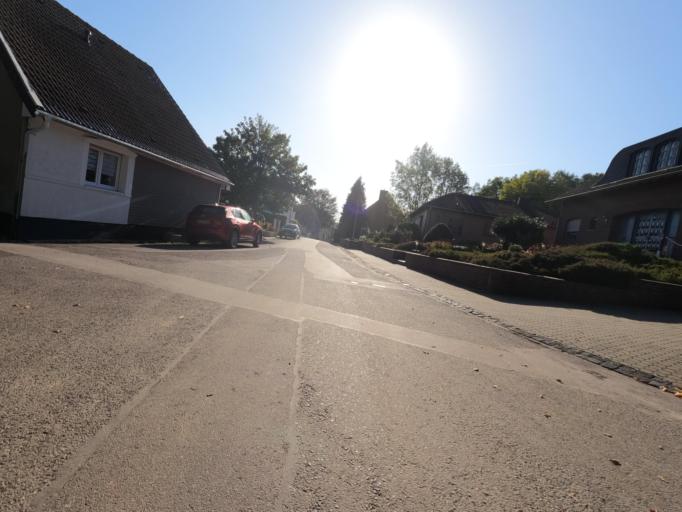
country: DE
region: North Rhine-Westphalia
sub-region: Regierungsbezirk Koln
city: Linnich
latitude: 50.9617
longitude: 6.2544
